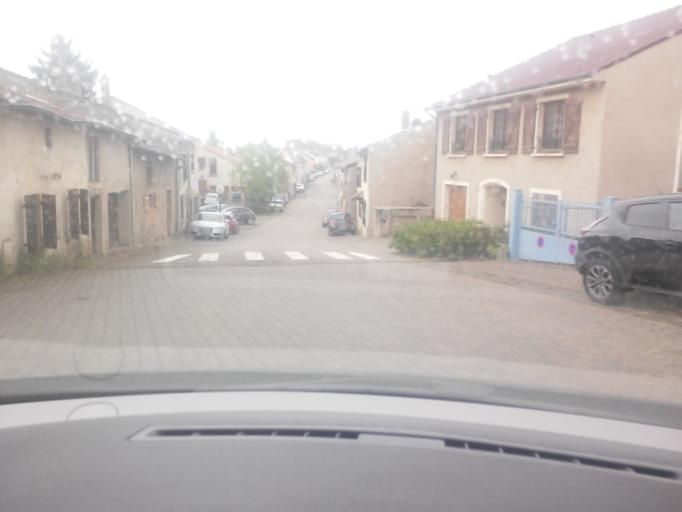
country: FR
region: Lorraine
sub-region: Departement de la Moselle
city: Verny
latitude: 49.0129
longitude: 6.2352
